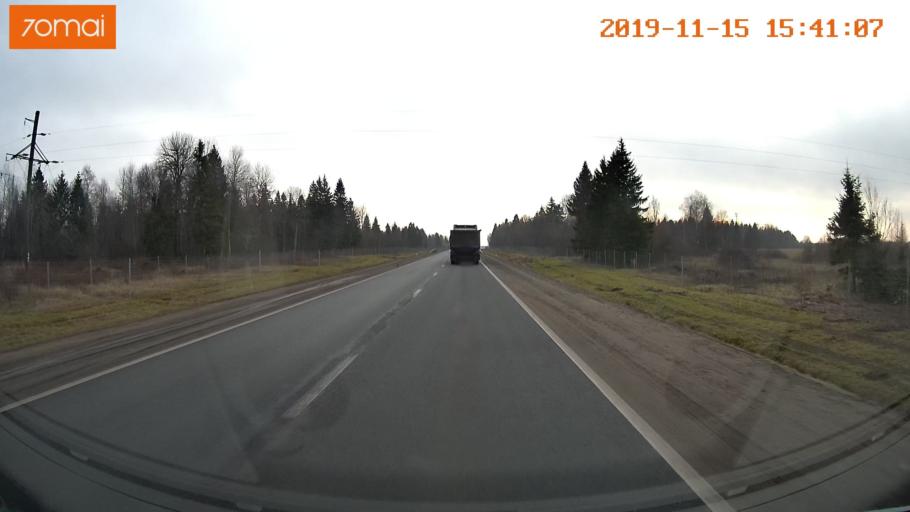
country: RU
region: Jaroslavl
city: Danilov
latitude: 58.0042
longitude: 40.0508
